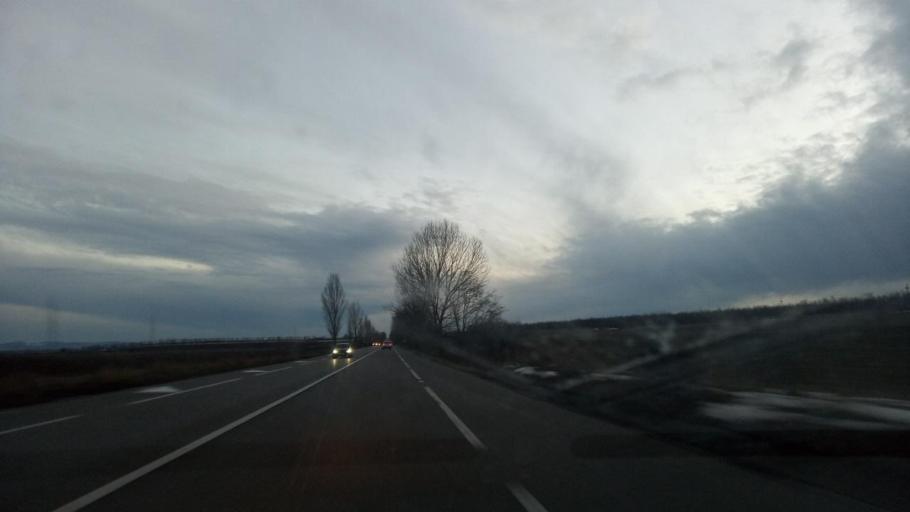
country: RO
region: Bacau
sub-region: Comuna Filipesti
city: Filipesti
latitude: 46.7181
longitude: 26.8894
